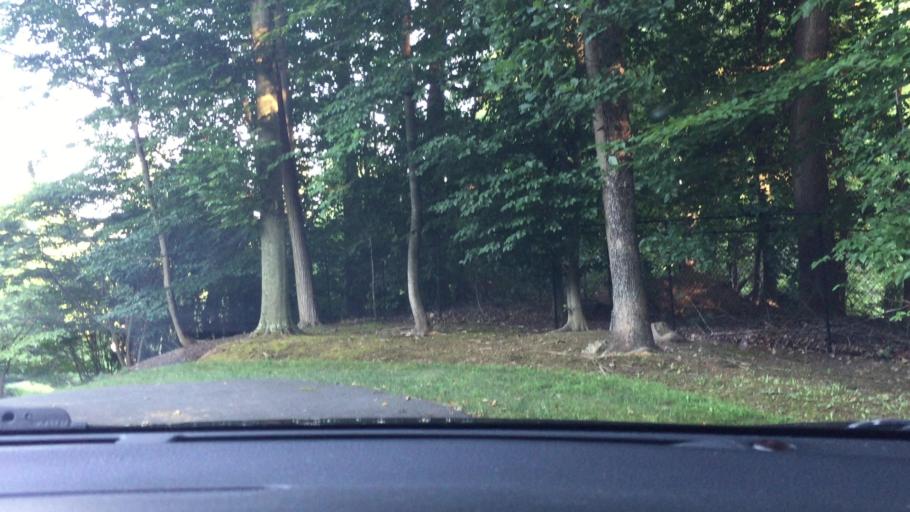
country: US
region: Maryland
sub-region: Montgomery County
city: Cabin John
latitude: 39.0103
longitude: -77.1628
